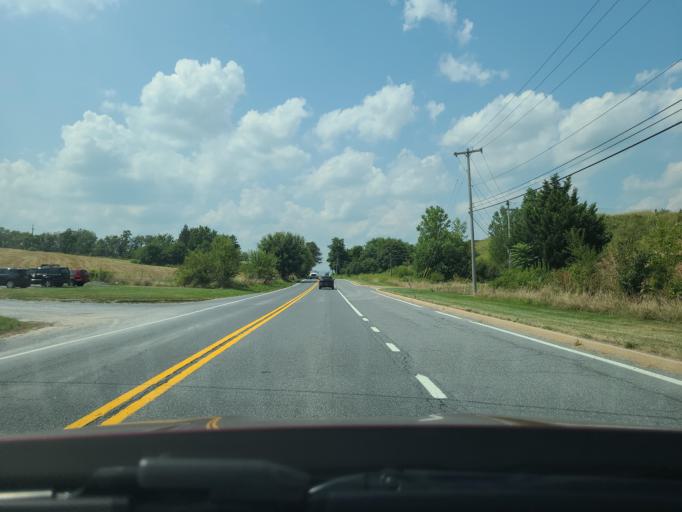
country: US
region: Maryland
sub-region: Frederick County
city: Woodsboro
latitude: 39.5456
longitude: -77.3261
